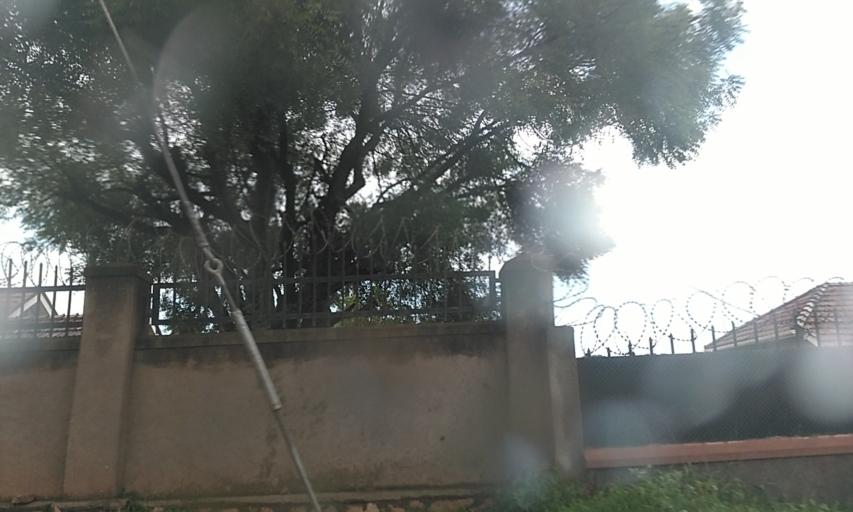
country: UG
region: Central Region
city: Kampala Central Division
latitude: 0.3424
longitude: 32.5944
